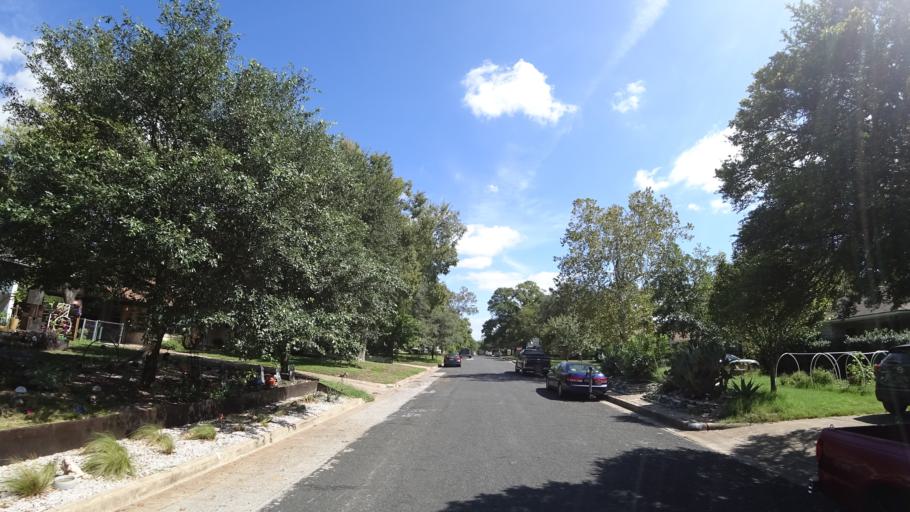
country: US
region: Texas
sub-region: Travis County
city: Austin
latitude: 30.3448
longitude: -97.7246
